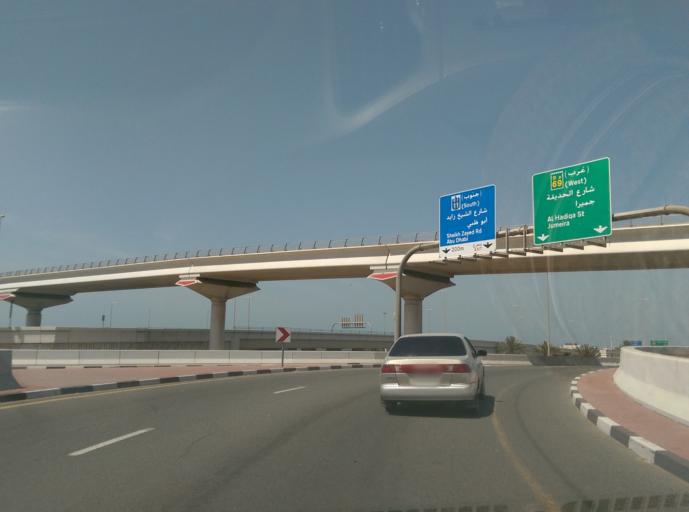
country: AE
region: Dubai
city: Dubai
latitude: 25.1803
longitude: 55.2511
